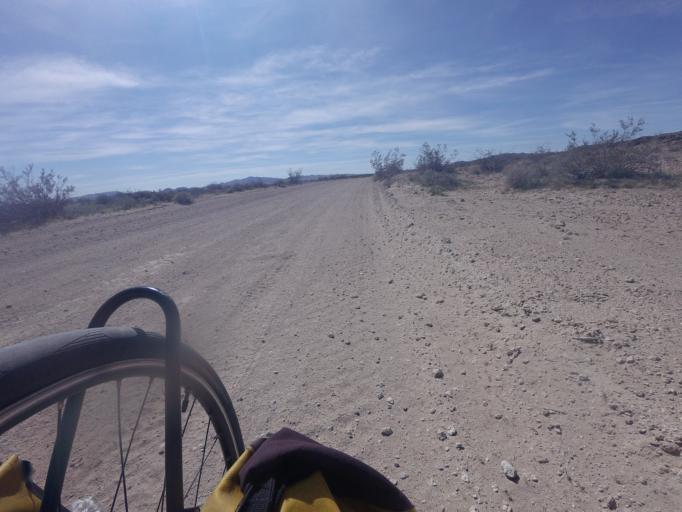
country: US
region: California
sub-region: San Bernardino County
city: Searles Valley
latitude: 35.5764
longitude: -117.4321
